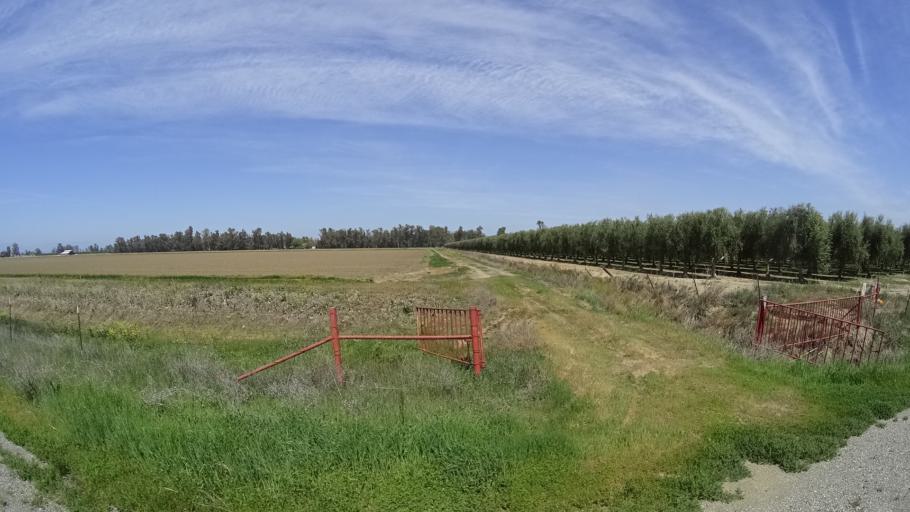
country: US
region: California
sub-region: Glenn County
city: Willows
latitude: 39.5762
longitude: -122.1978
